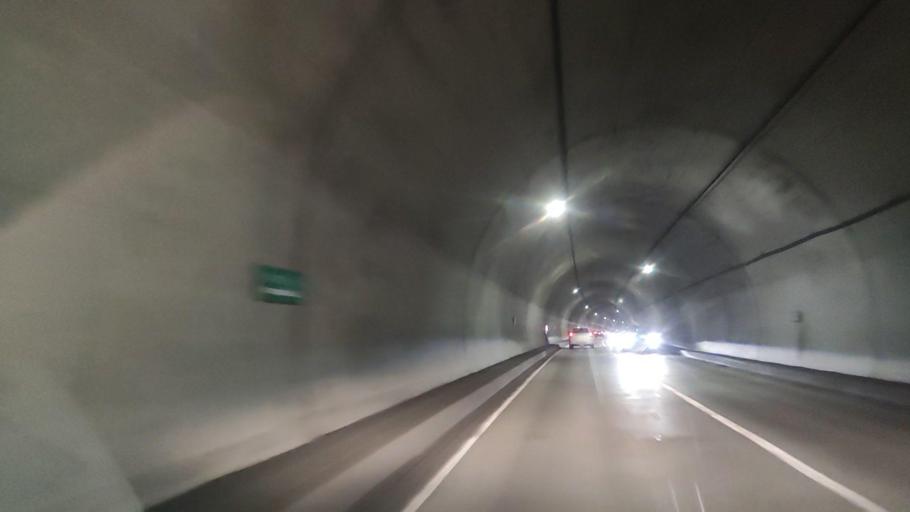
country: JP
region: Hokkaido
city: Ishikari
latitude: 43.5236
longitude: 141.3932
